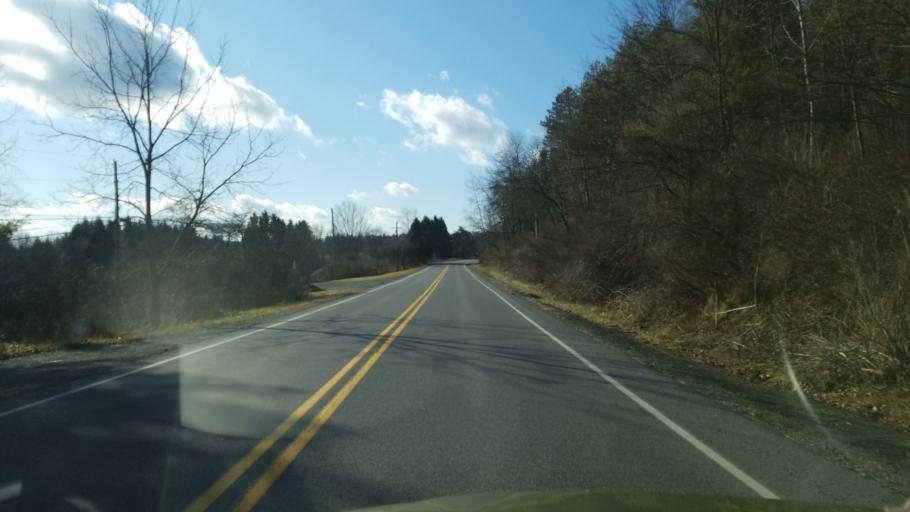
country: US
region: Pennsylvania
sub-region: Clearfield County
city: Hyde
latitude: 40.9869
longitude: -78.4436
